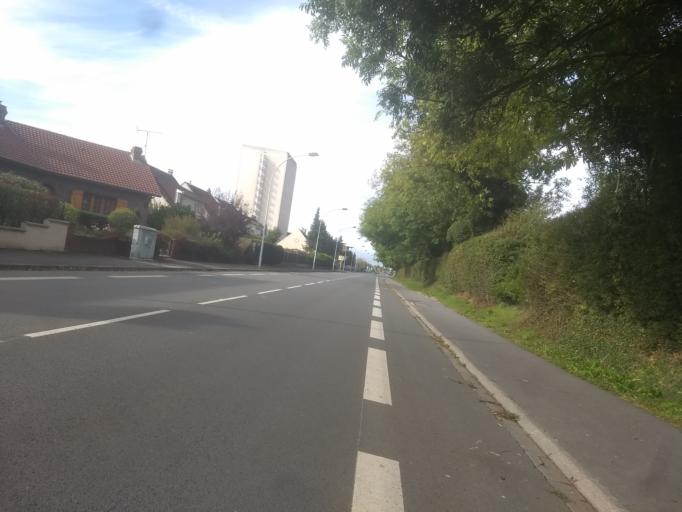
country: FR
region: Nord-Pas-de-Calais
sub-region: Departement du Pas-de-Calais
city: Dainville
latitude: 50.2926
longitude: 2.7403
